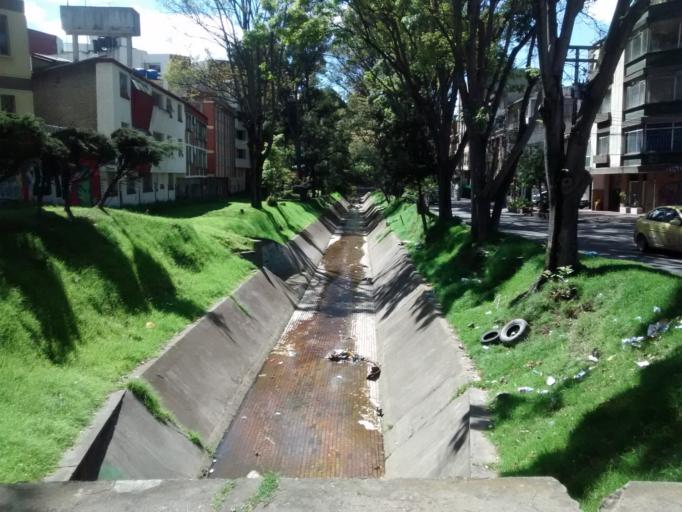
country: CO
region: Bogota D.C.
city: Bogota
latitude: 4.6343
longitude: -74.0754
